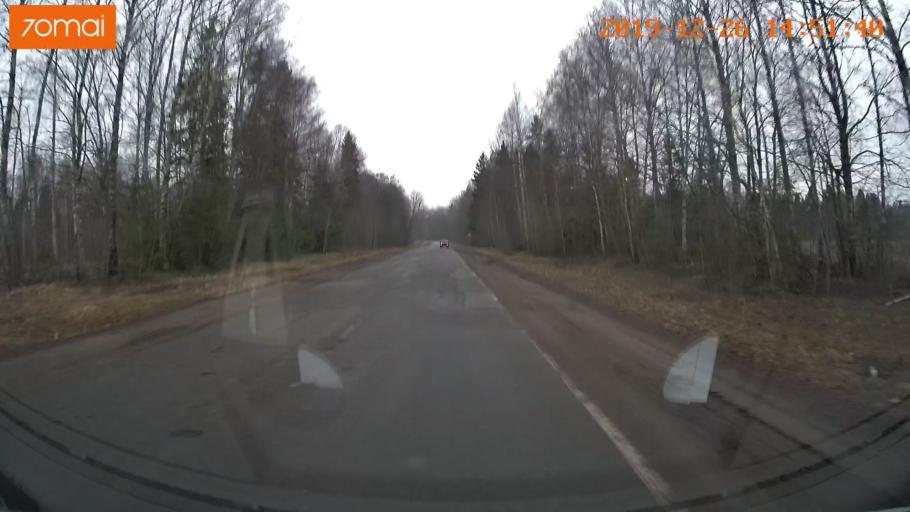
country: RU
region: Jaroslavl
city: Poshekhon'ye
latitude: 58.3250
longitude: 38.9079
